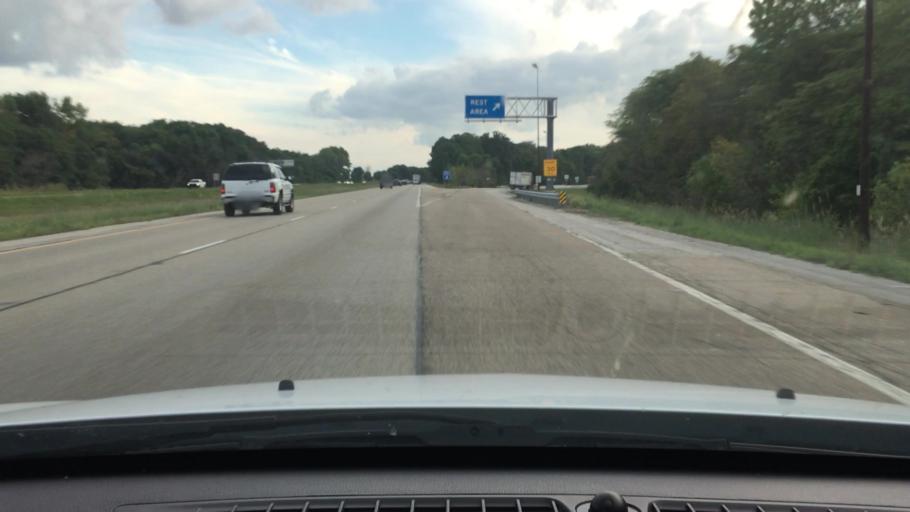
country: US
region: Illinois
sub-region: McLean County
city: Twin Grove
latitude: 40.3613
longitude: -89.1067
